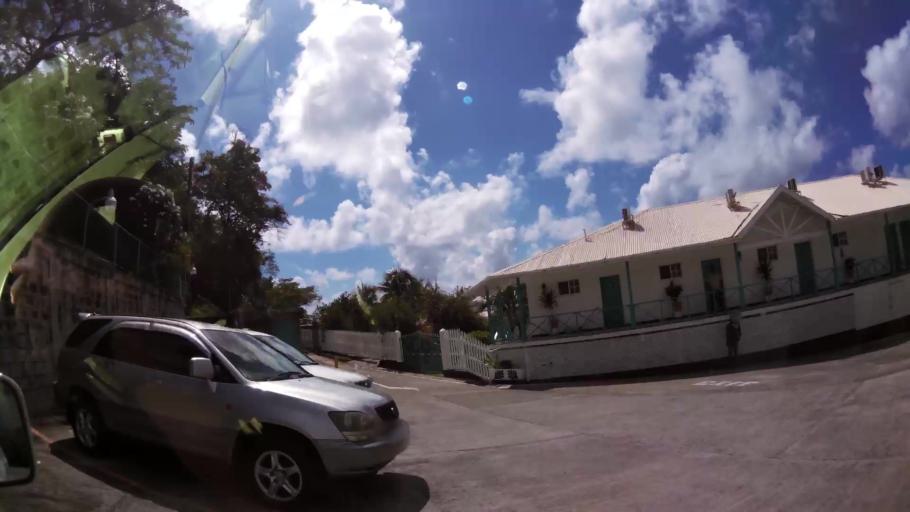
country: VC
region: Saint George
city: Kingstown
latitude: 13.1323
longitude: -61.1994
